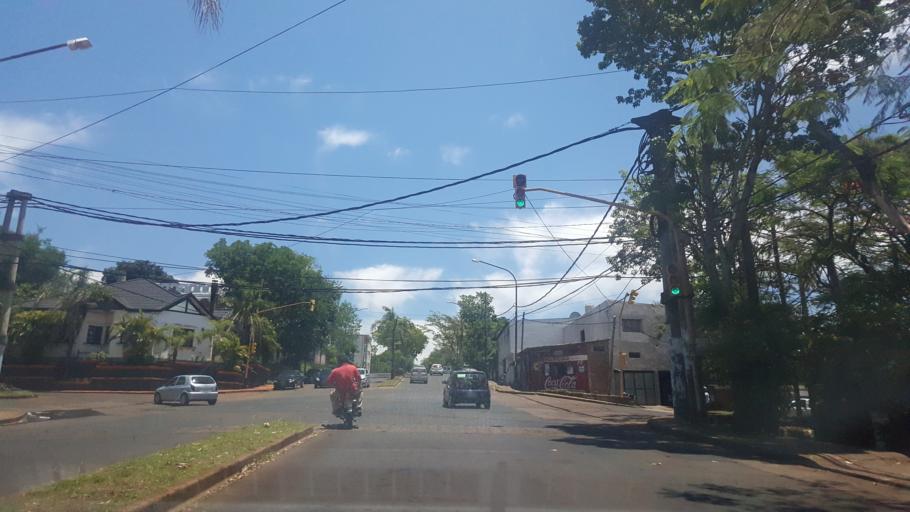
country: AR
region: Misiones
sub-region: Departamento de Capital
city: Posadas
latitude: -27.3627
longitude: -55.9114
